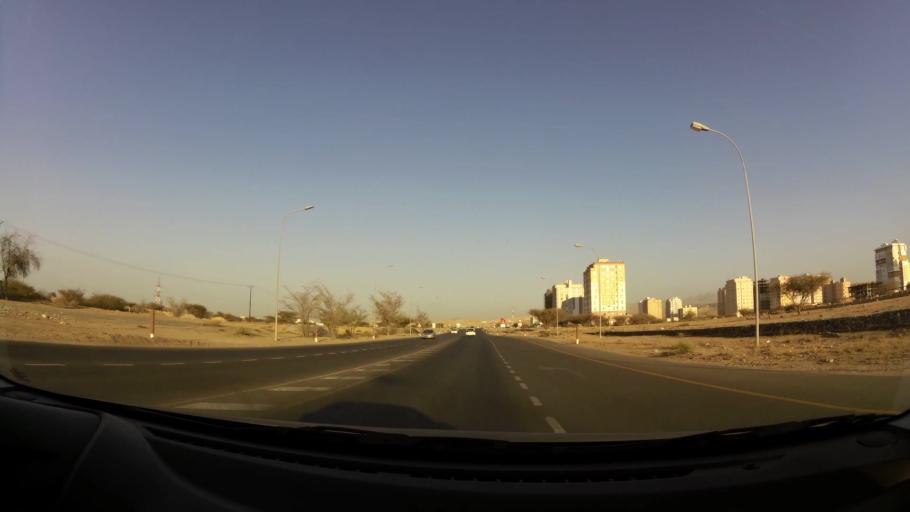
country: OM
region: Muhafazat Masqat
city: As Sib al Jadidah
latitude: 23.5783
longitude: 58.1787
